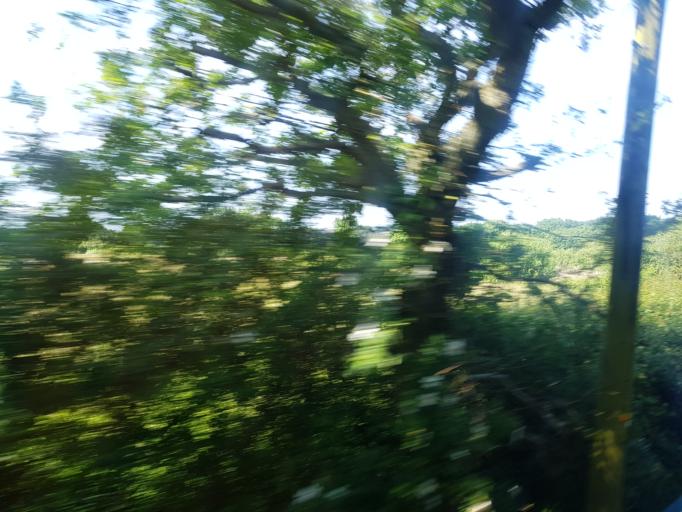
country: GB
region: England
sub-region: Isle of Wight
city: Newport
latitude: 50.7095
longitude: -1.2573
